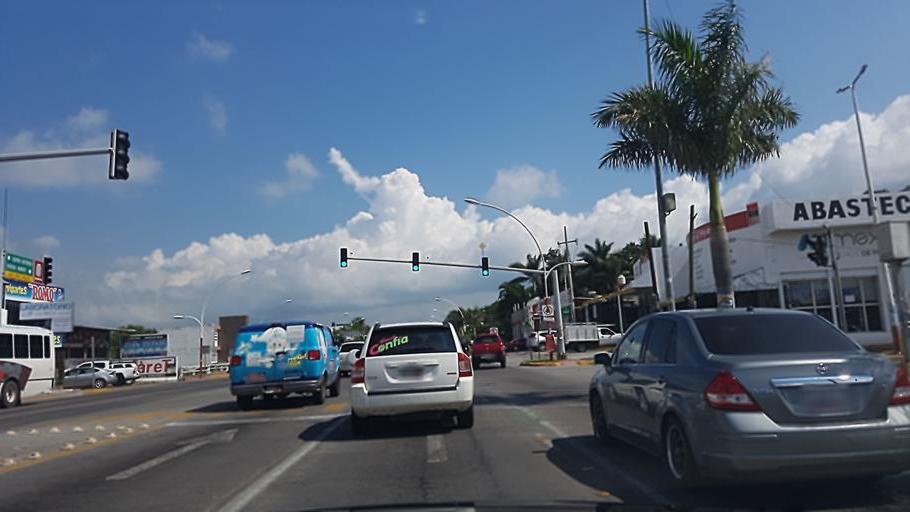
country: MX
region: Nayarit
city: Xalisco
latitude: 21.4792
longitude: -104.8917
